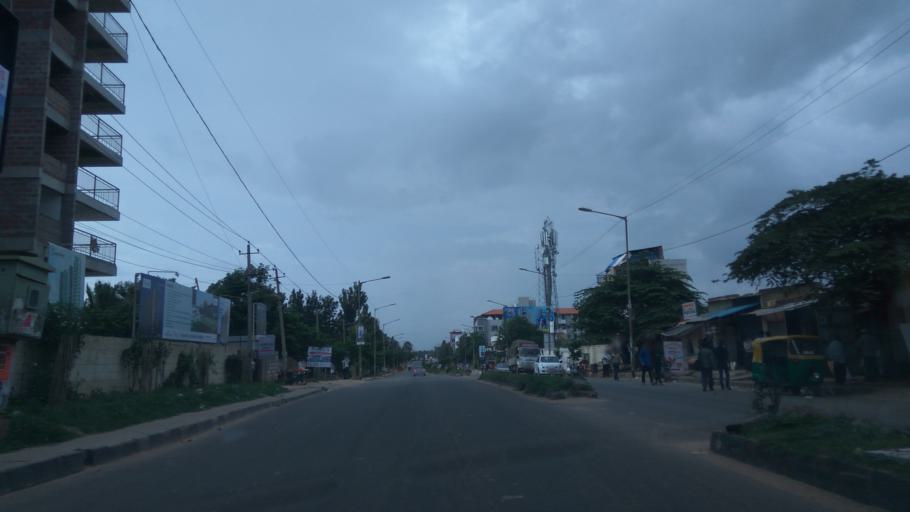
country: IN
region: Karnataka
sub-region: Bangalore Urban
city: Yelahanka
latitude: 13.0799
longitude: 77.6340
